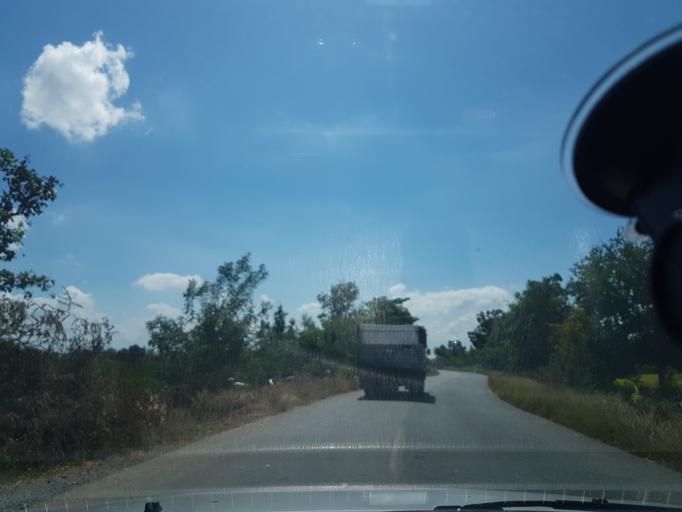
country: TH
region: Lop Buri
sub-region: Amphoe Tha Luang
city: Tha Luang
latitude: 14.9956
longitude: 101.0111
